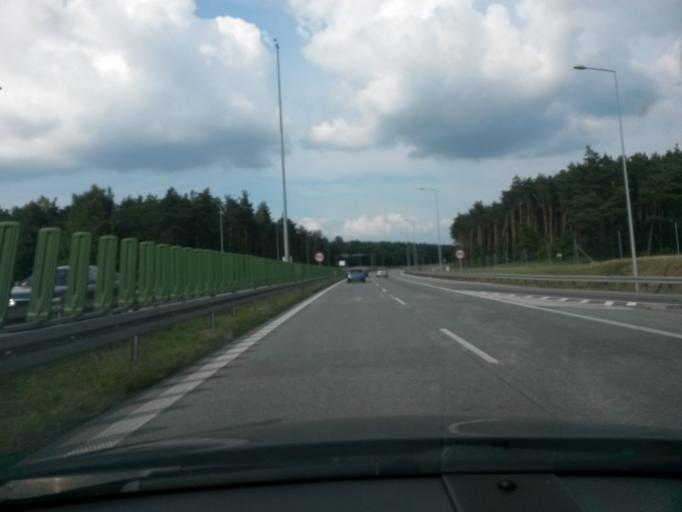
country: PL
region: Lodz Voivodeship
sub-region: Powiat tomaszowski
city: Lubochnia
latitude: 51.6249
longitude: 20.0966
